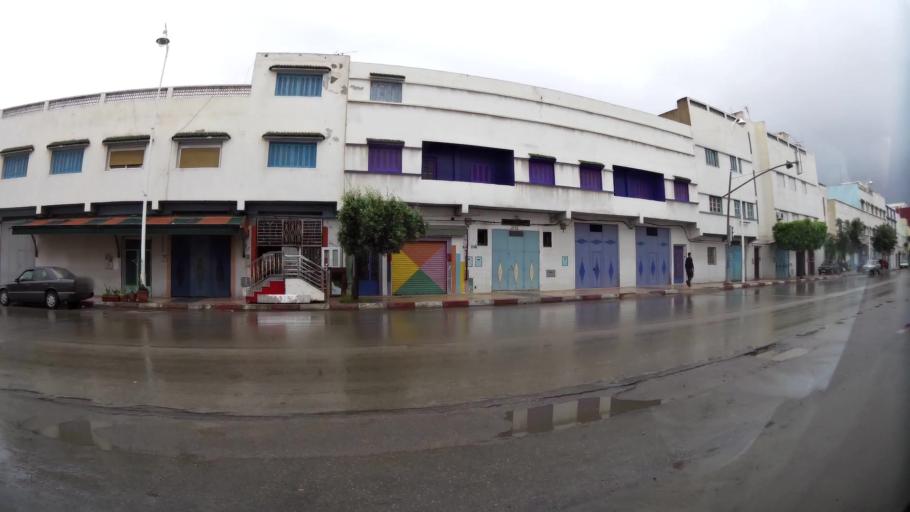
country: MA
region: Oriental
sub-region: Nador
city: Nador
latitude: 35.1549
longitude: -2.9785
